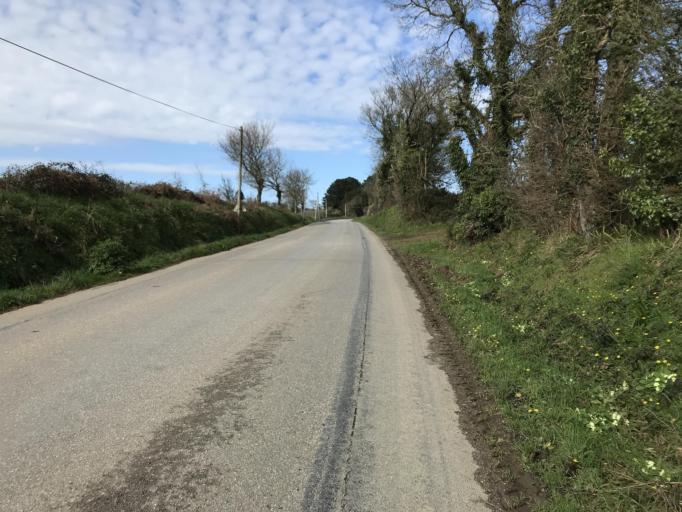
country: FR
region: Brittany
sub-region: Departement du Finistere
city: Daoulas
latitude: 48.3624
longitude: -4.2762
